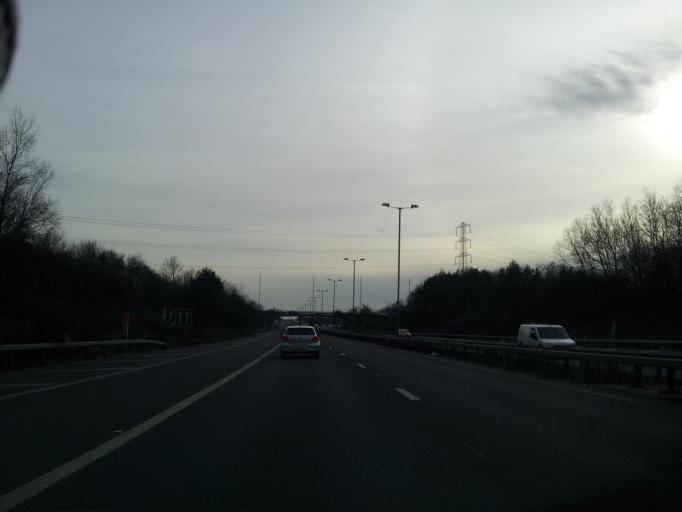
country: GB
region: England
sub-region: Greater London
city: High Barnet
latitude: 51.6863
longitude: -0.2293
